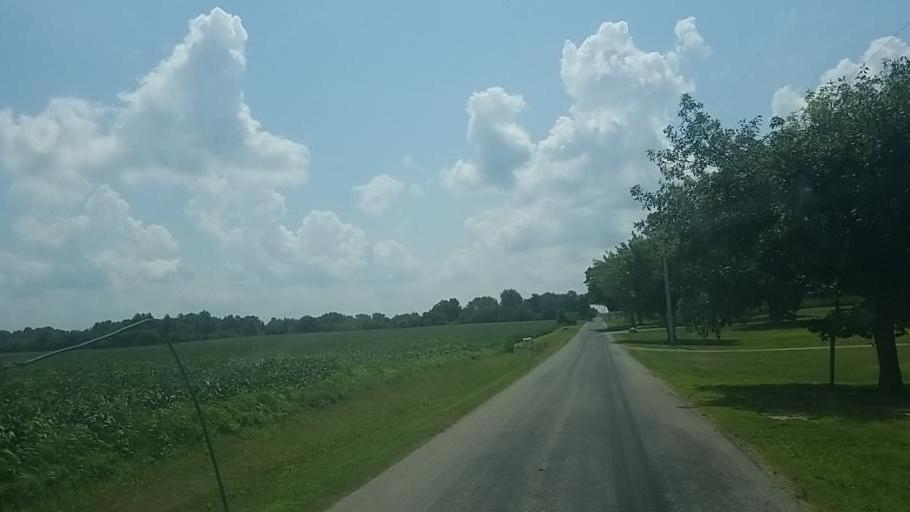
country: US
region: Ohio
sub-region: Marion County
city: Marion
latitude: 40.7291
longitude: -83.1499
